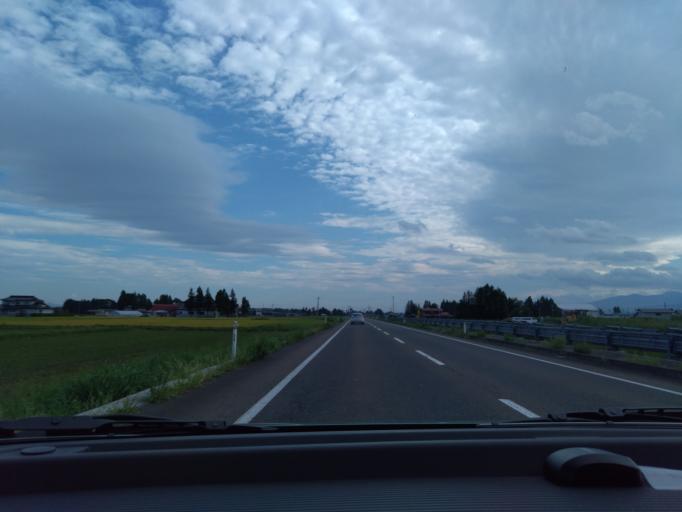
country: JP
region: Iwate
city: Hanamaki
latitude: 39.3675
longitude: 141.0569
